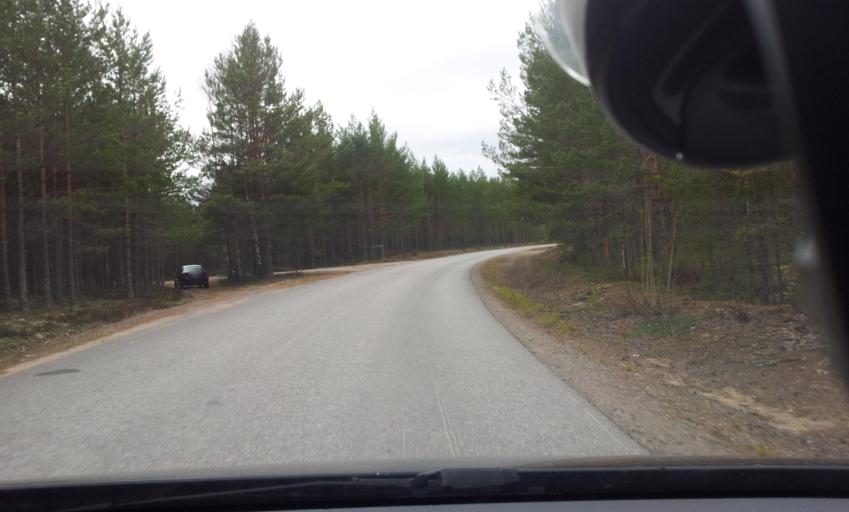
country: SE
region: Gaevleborg
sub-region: Ljusdals Kommun
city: Ljusdal
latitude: 61.8323
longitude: 16.0178
